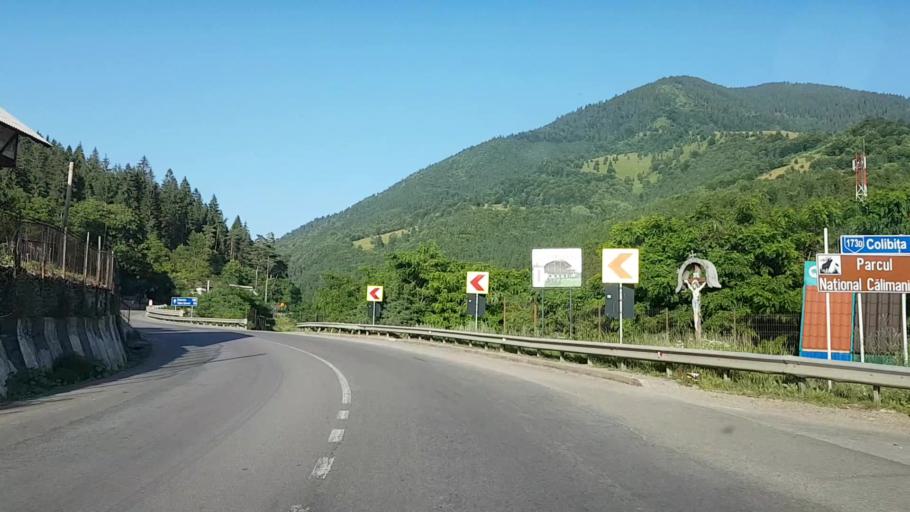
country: RO
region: Bistrita-Nasaud
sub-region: Comuna Tiha Bargaului
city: Tureac
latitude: 47.2096
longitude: 24.8692
